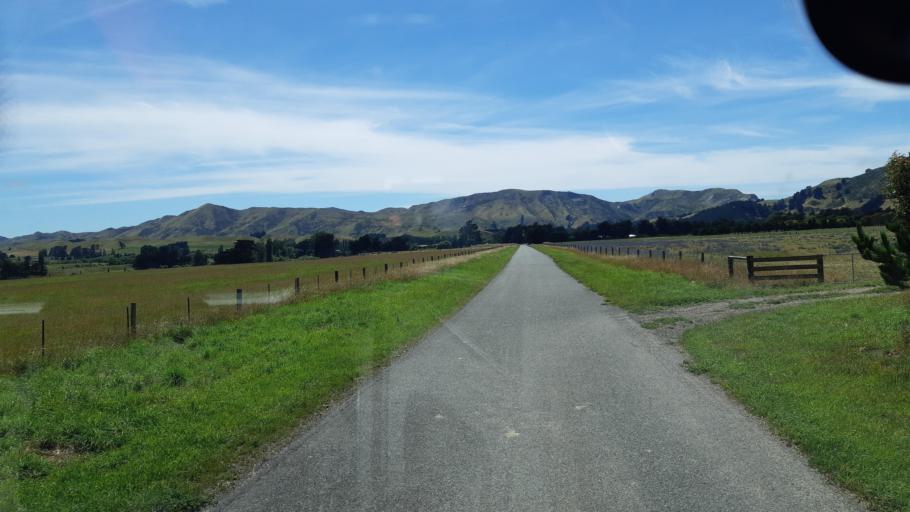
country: NZ
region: Marlborough
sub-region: Marlborough District
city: Blenheim
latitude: -41.8282
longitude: 174.1205
